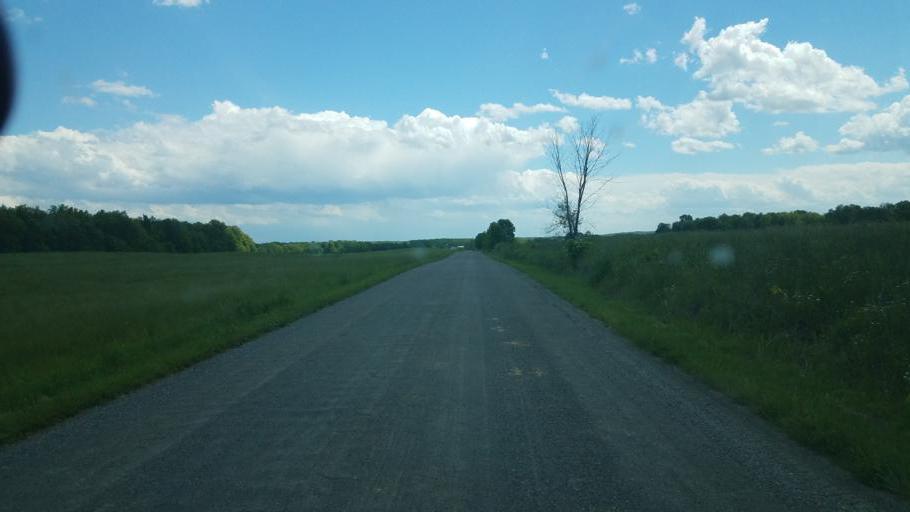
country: US
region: Ohio
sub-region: Geauga County
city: Middlefield
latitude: 41.4008
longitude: -80.9901
